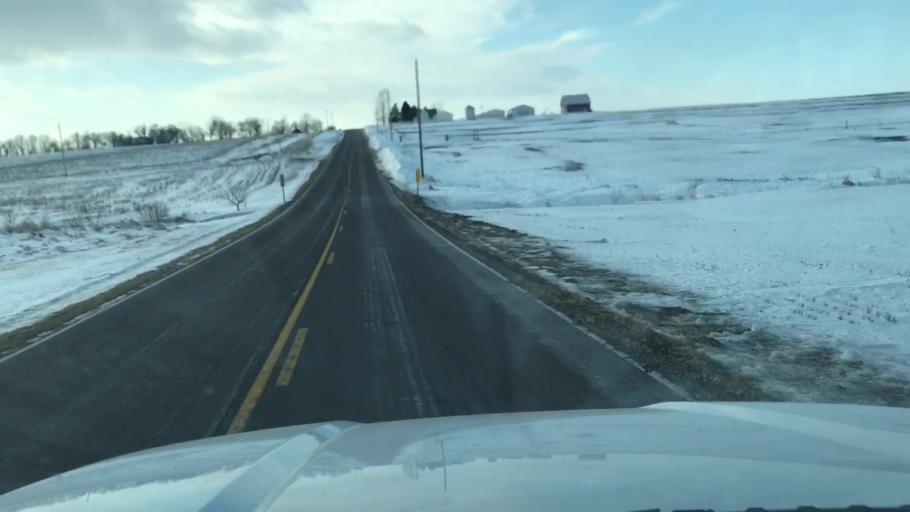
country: US
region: Missouri
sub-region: Nodaway County
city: Maryville
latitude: 40.2012
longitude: -94.9140
